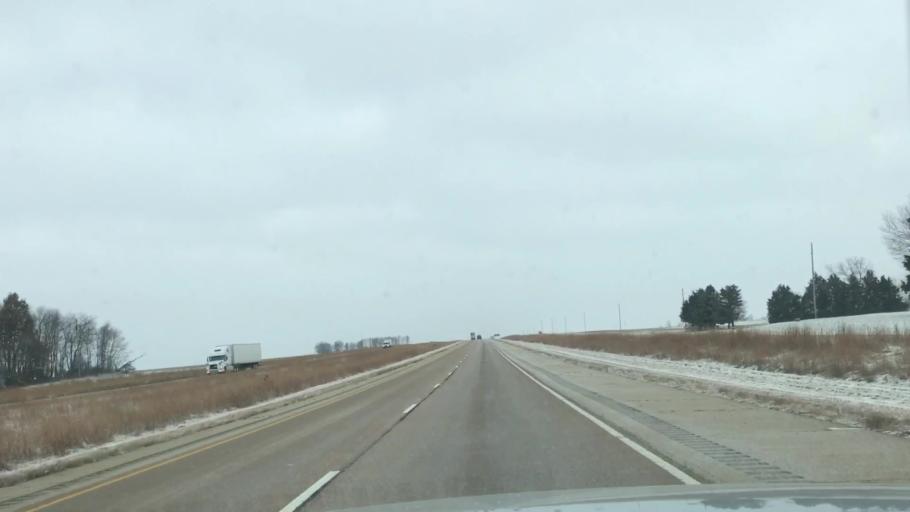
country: US
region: Illinois
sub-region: Montgomery County
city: Raymond
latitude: 39.2951
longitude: -89.6419
